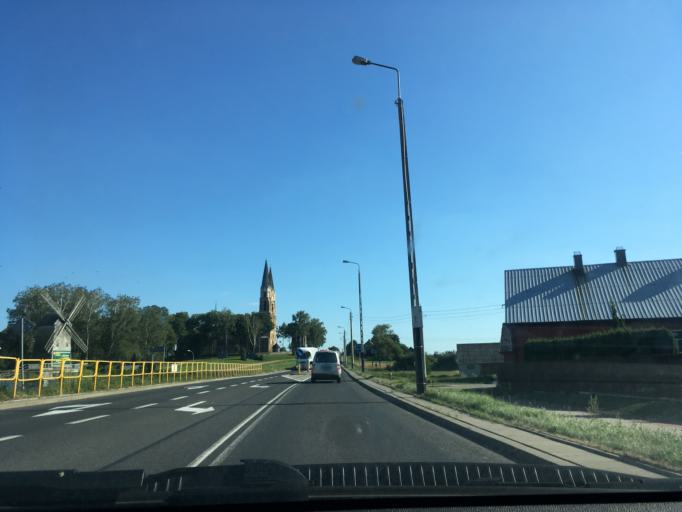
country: PL
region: Podlasie
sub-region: Powiat sokolski
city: Suchowola
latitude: 53.4439
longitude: 23.0945
